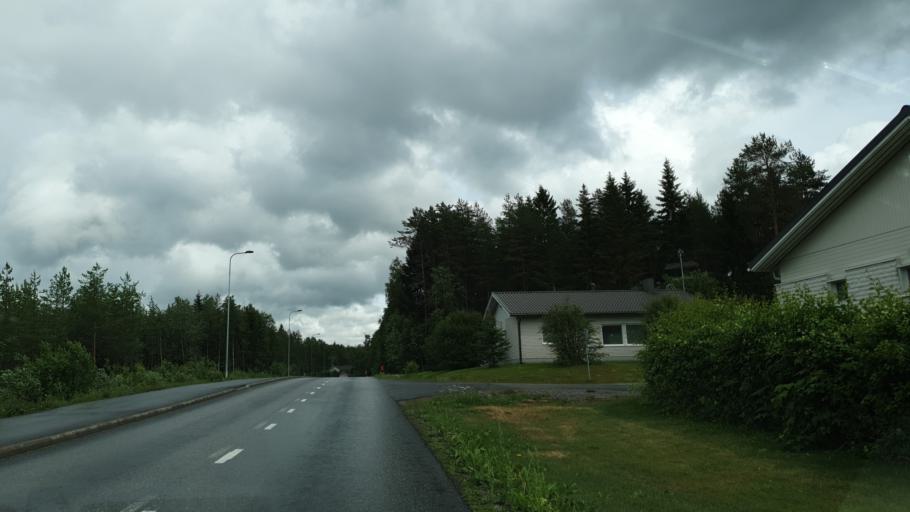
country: FI
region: Kainuu
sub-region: Kehys-Kainuu
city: Kuhmo
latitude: 64.1194
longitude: 29.4905
